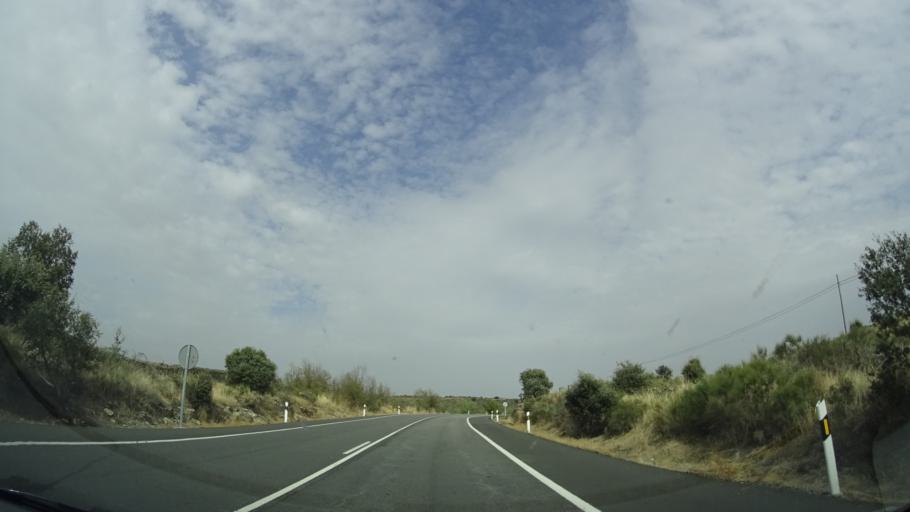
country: ES
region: Extremadura
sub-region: Provincia de Caceres
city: Trujillo
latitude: 39.4331
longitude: -5.8918
